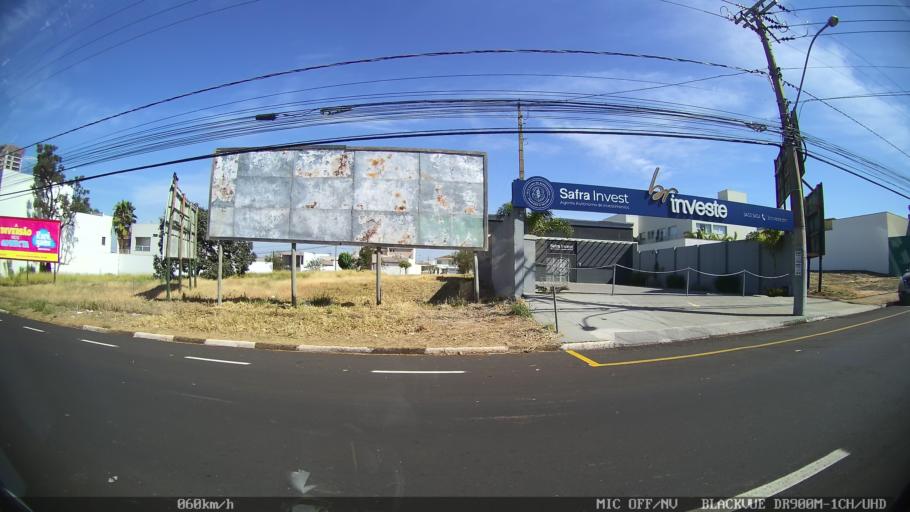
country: BR
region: Sao Paulo
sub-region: Franca
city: Franca
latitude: -20.5500
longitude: -47.4164
